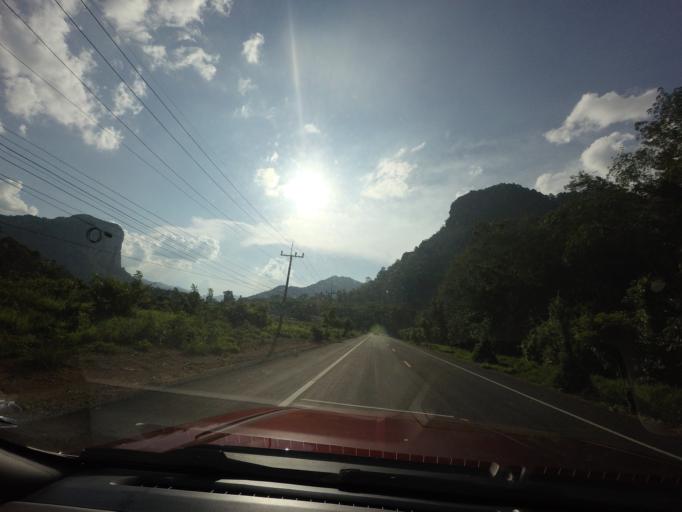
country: TH
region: Yala
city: Ban Nang Sata
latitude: 6.2328
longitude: 101.2155
